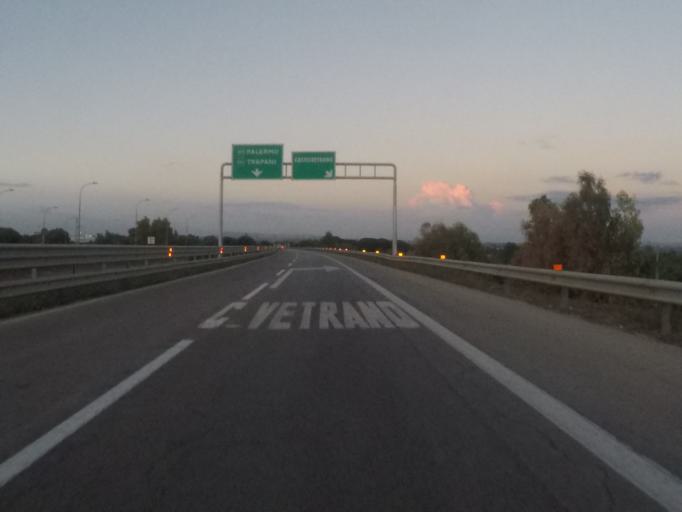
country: IT
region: Sicily
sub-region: Trapani
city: Castelvetrano
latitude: 37.6618
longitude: 12.8129
